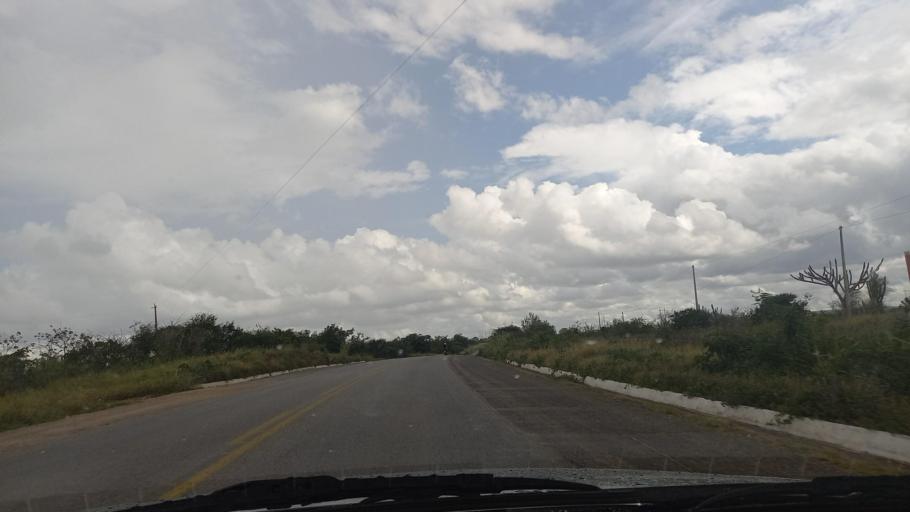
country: BR
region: Pernambuco
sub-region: Cachoeirinha
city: Cachoeirinha
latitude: -8.5616
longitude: -36.2768
